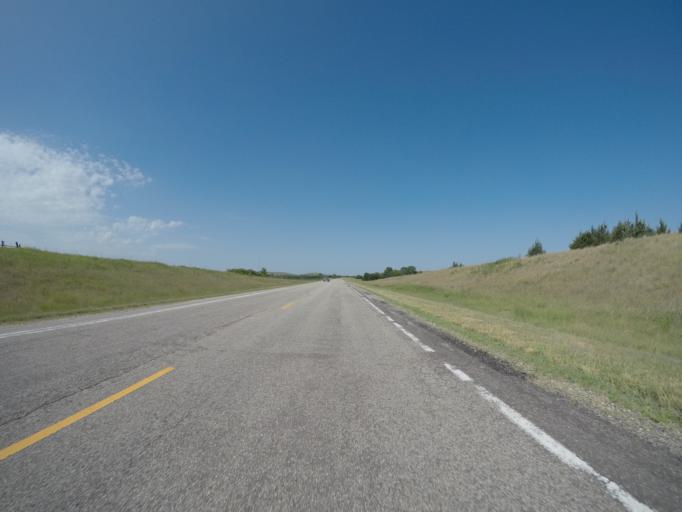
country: US
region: Kansas
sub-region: Clay County
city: Clay Center
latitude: 39.3757
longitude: -97.3926
